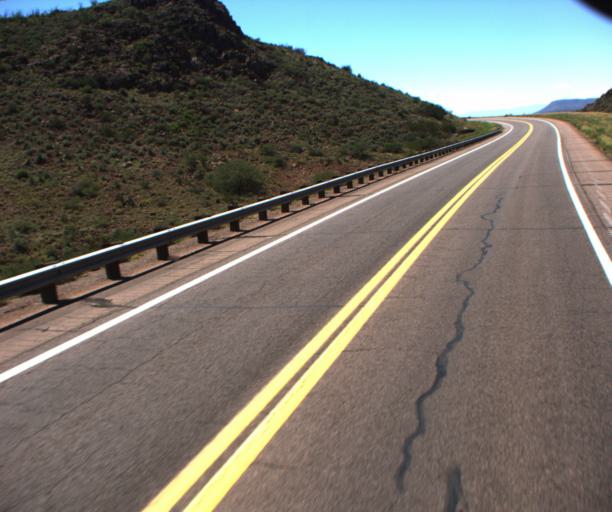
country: US
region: Arizona
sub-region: Greenlee County
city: Clifton
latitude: 32.8472
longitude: -109.3932
